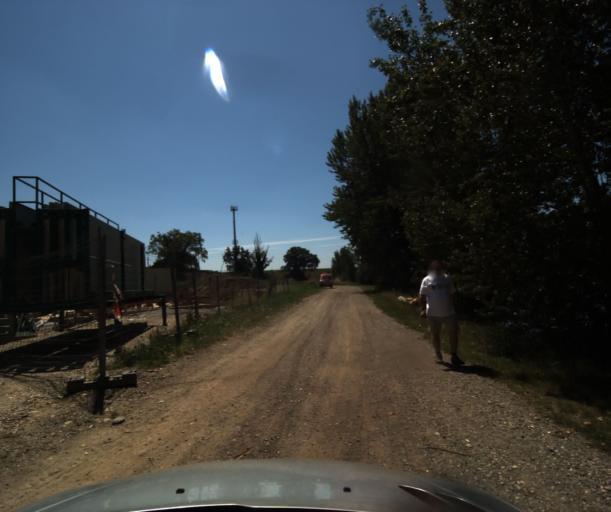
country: FR
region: Midi-Pyrenees
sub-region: Departement de la Haute-Garonne
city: Roquettes
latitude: 43.4926
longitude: 1.3675
